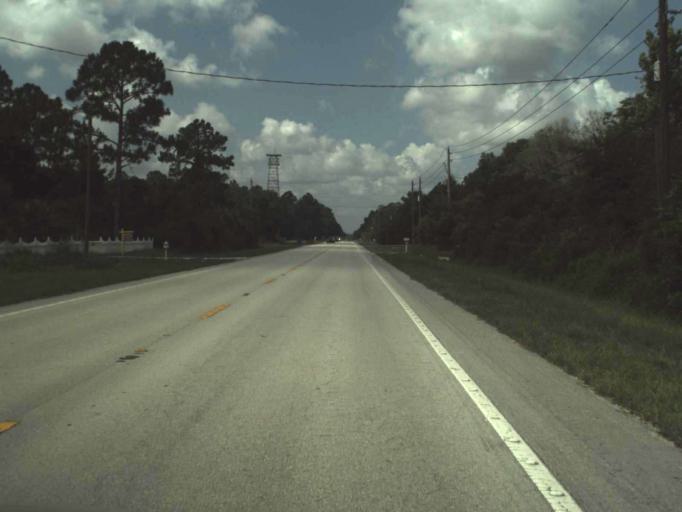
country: US
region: Florida
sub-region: Volusia County
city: Samsula-Spruce Creek
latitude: 28.9615
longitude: -81.0898
